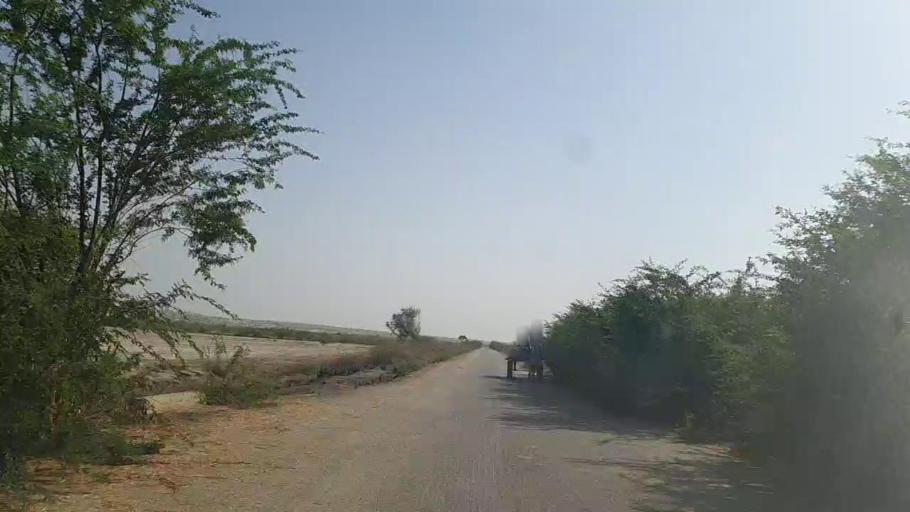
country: PK
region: Sindh
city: Kadhan
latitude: 24.5606
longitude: 69.2764
